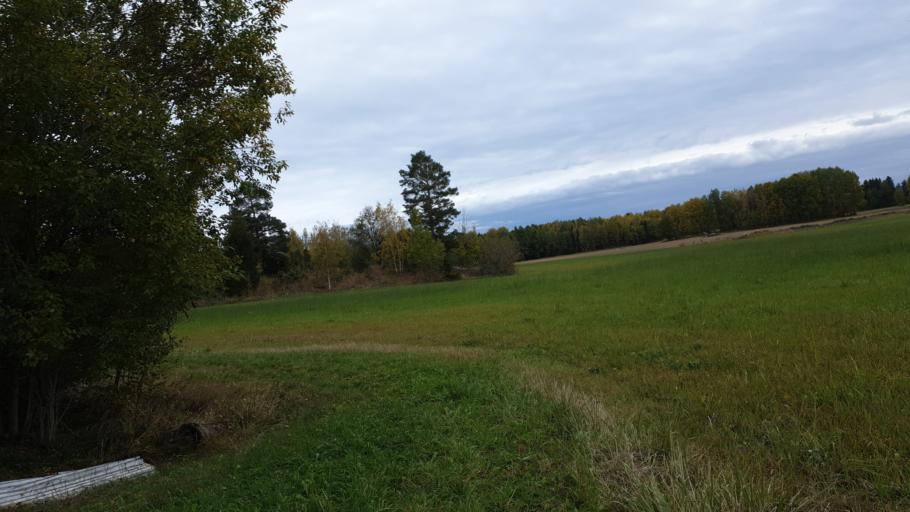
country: SE
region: Vaestmanland
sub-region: Sala Kommun
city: Sala
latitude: 59.8155
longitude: 16.6499
